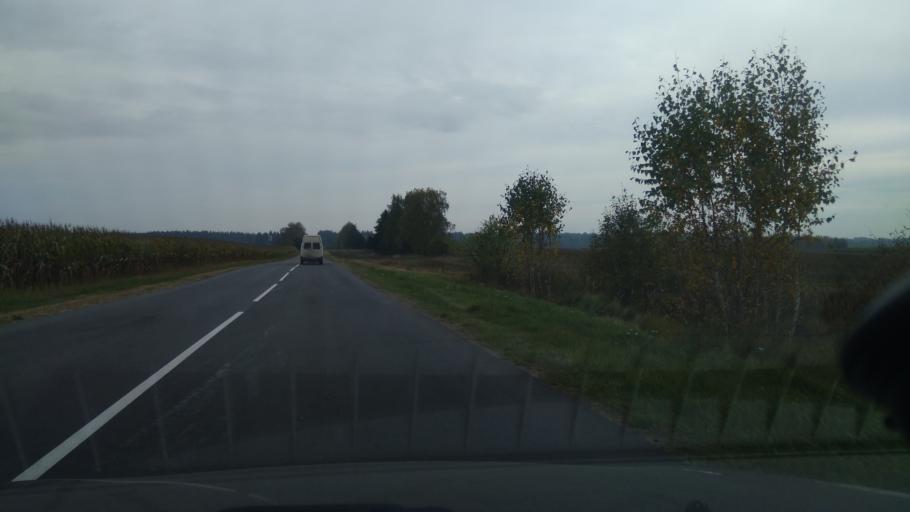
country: BY
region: Minsk
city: Rudzyensk
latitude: 53.6147
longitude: 27.7559
